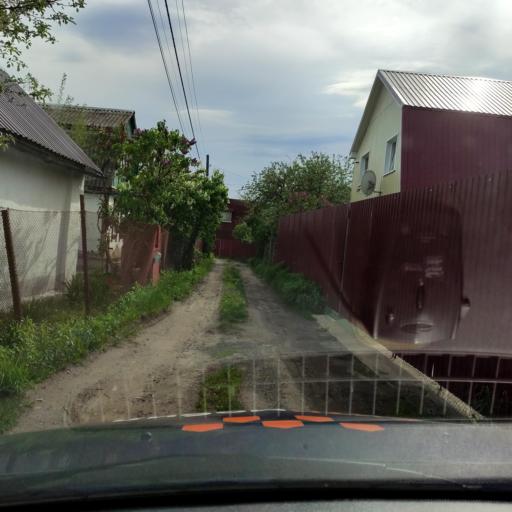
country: RU
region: Voronezj
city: Shilovo
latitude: 51.5977
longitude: 39.1459
